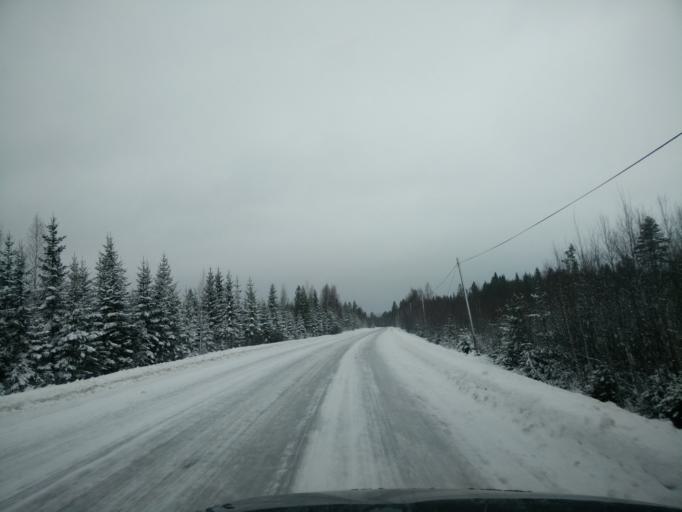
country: SE
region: Vaesternorrland
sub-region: Ange Kommun
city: Ange
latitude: 62.4010
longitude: 15.3220
